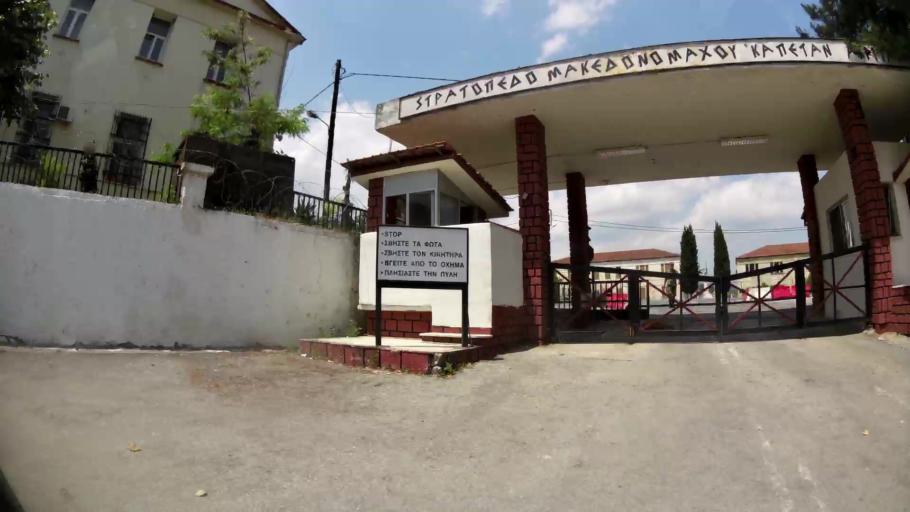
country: GR
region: Central Macedonia
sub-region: Nomos Imathias
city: Veroia
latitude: 40.5162
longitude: 22.1948
